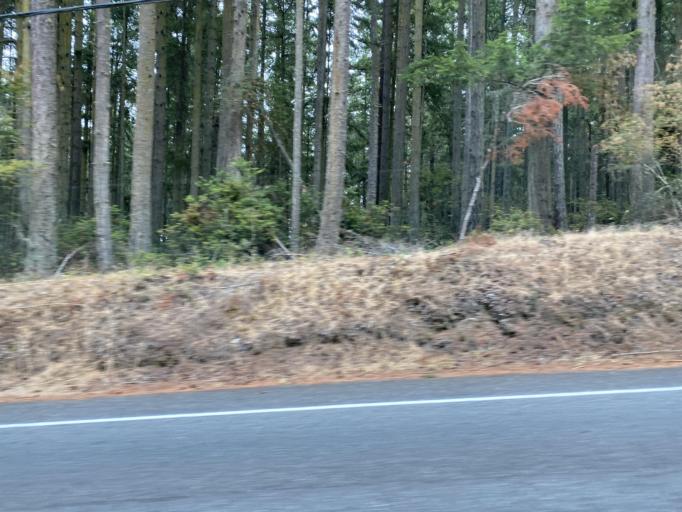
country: US
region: Washington
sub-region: Island County
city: Coupeville
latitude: 48.2153
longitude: -122.6359
